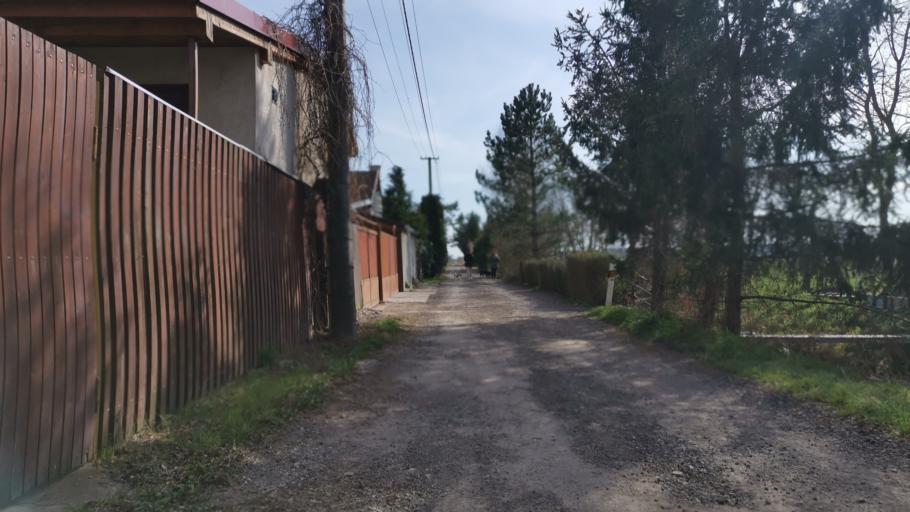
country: CZ
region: South Moravian
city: Tvrdonice
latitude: 48.7305
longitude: 17.0245
